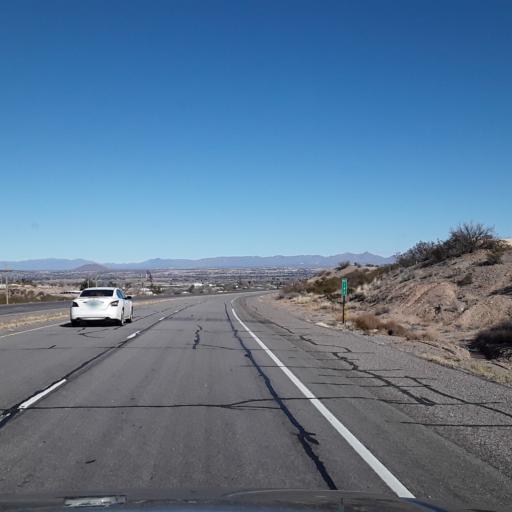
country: US
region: New Mexico
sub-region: Dona Ana County
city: Mesilla
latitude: 32.2886
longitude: -106.8733
